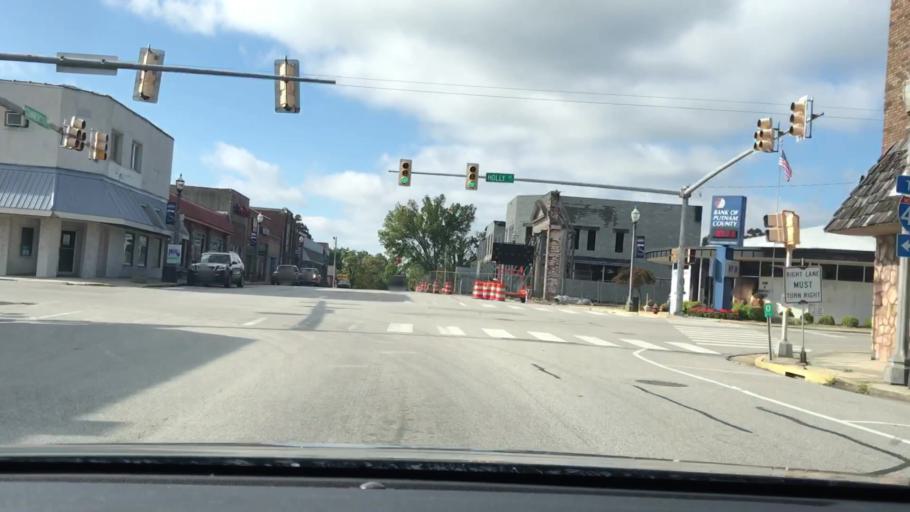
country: US
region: Tennessee
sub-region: Putnam County
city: Monterey
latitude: 36.1476
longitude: -85.2678
